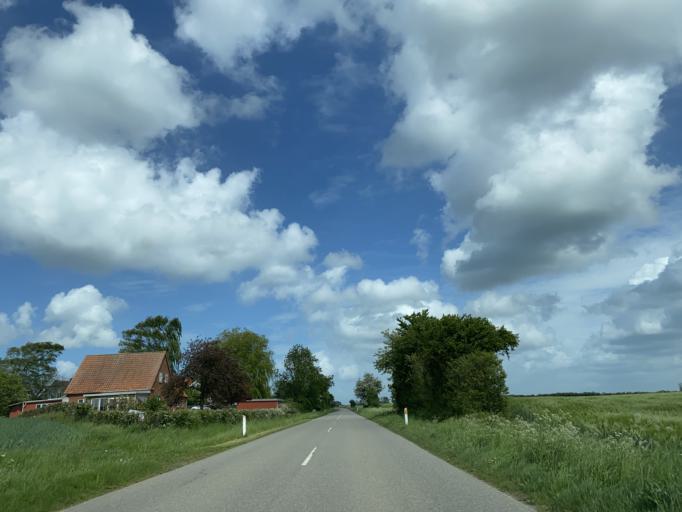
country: DK
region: South Denmark
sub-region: Sonderborg Kommune
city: Dybbol
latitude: 54.9699
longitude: 9.7082
